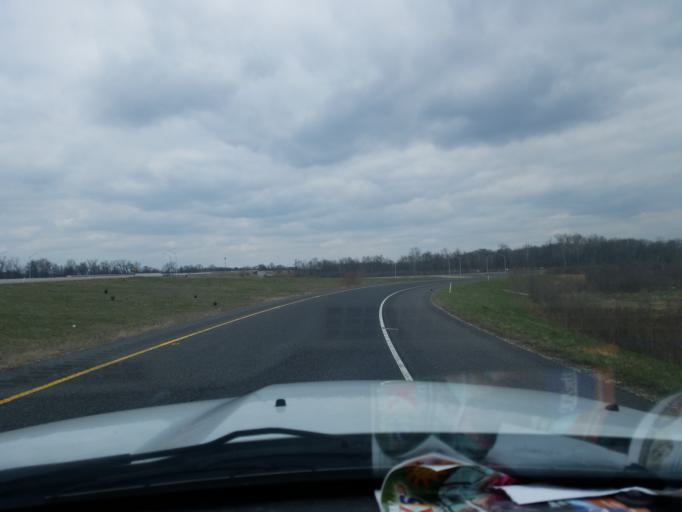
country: US
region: Indiana
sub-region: Vigo County
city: Terre Haute
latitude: 39.3955
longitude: -87.3725
